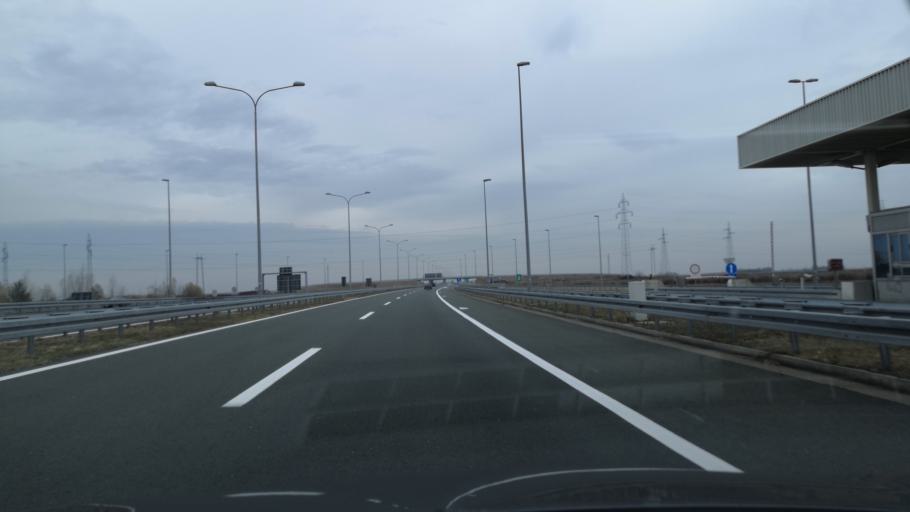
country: RS
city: Rumenka
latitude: 45.3132
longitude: 19.7997
